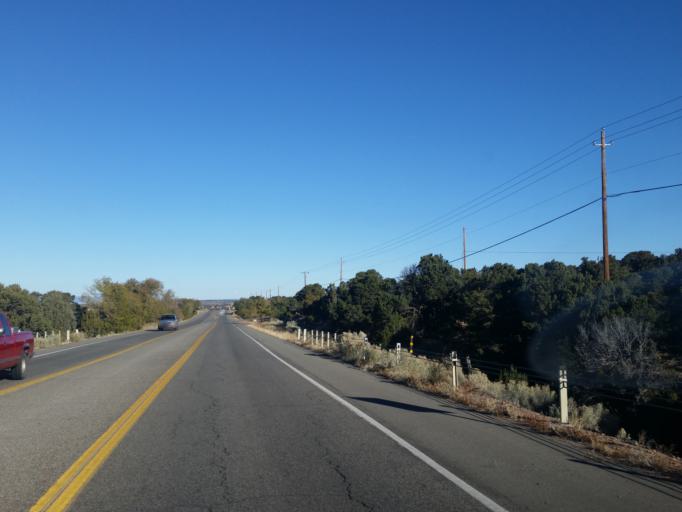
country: US
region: New Mexico
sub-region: Santa Fe County
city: Santa Fe
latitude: 35.6306
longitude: -105.9235
